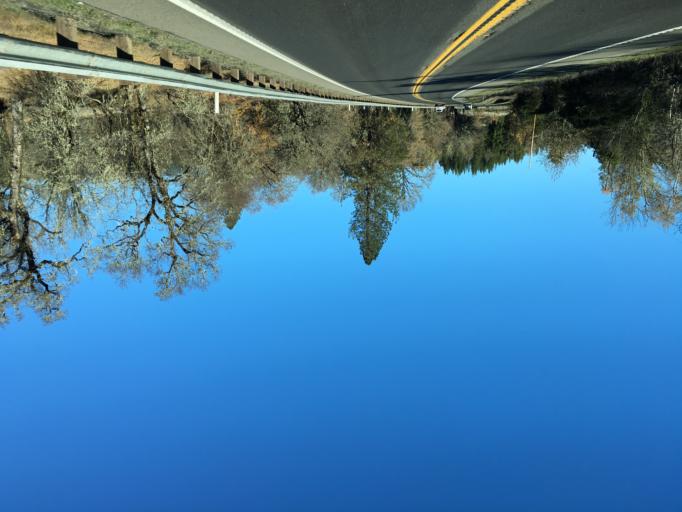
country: US
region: California
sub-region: Mendocino County
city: Laytonville
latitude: 39.7376
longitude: -123.5139
